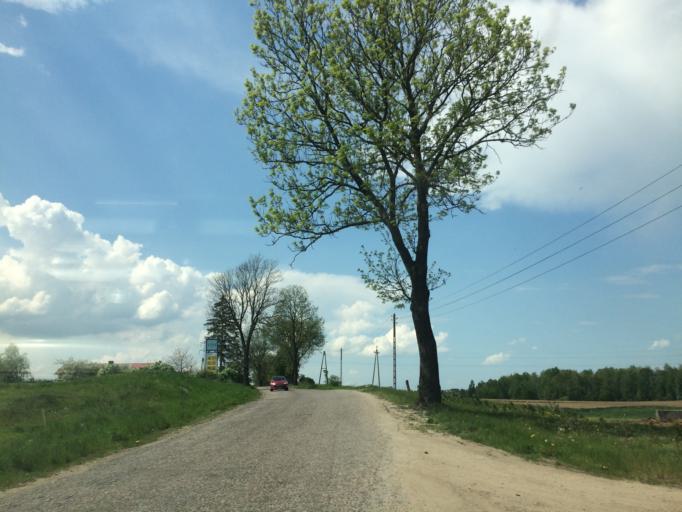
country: PL
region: Warmian-Masurian Voivodeship
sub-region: Powiat ilawski
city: Ilawa
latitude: 53.5337
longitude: 19.4732
